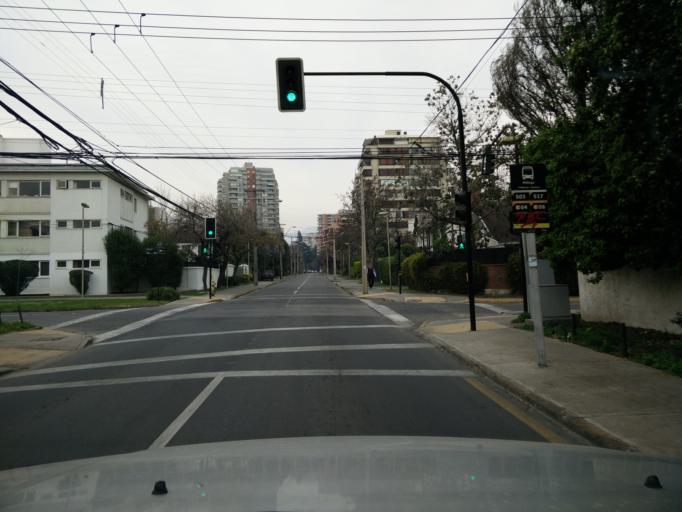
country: CL
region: Santiago Metropolitan
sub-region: Provincia de Santiago
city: Villa Presidente Frei, Nunoa, Santiago, Chile
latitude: -33.4227
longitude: -70.5842
